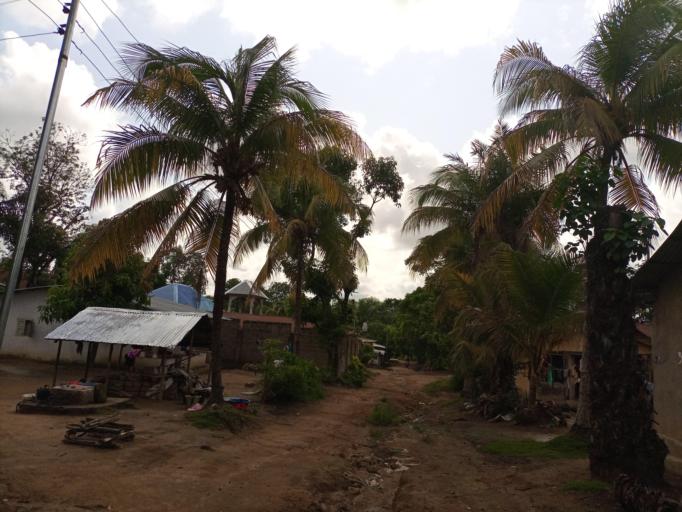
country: SL
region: Southern Province
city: Bo
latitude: 7.9661
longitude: -11.7621
